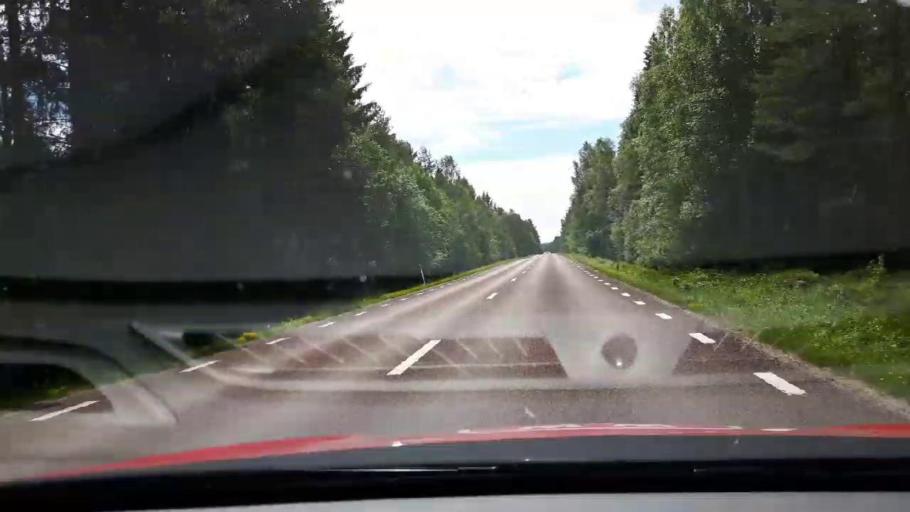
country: SE
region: Jaemtland
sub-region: Harjedalens Kommun
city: Sveg
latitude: 62.1162
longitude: 14.9701
